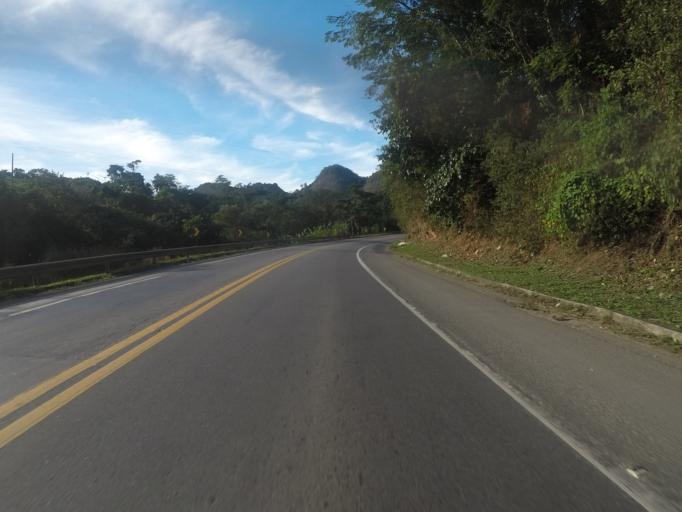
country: BR
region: Espirito Santo
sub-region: Ibiracu
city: Ibiracu
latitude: -19.8691
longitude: -40.4087
